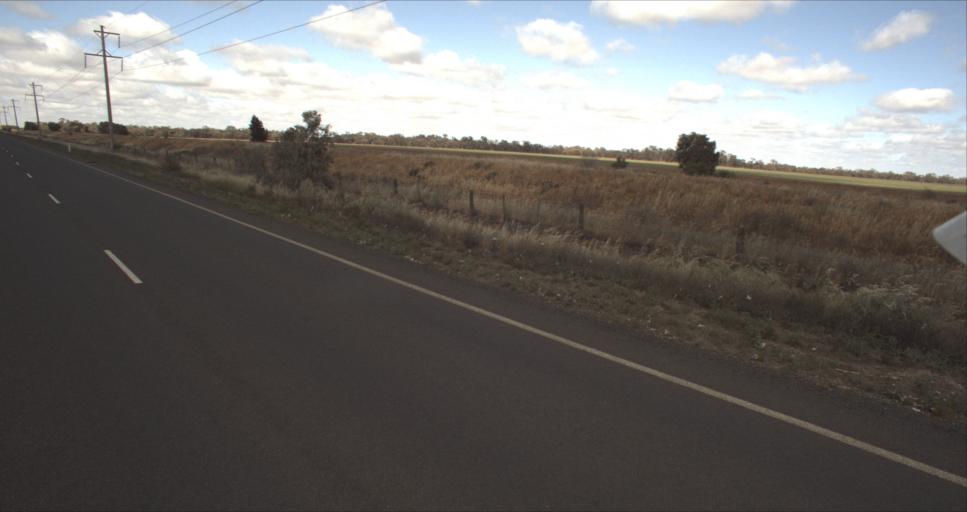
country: AU
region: New South Wales
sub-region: Murrumbidgee Shire
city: Darlington Point
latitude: -34.5357
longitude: 146.1731
